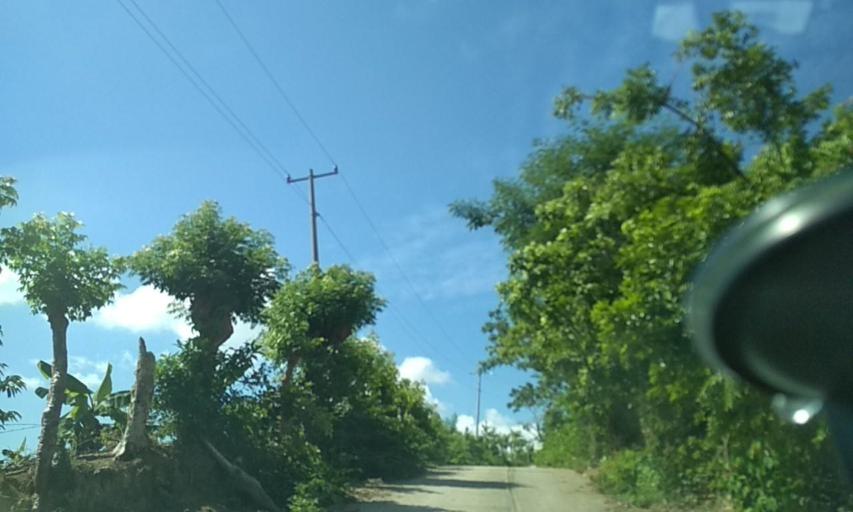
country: MX
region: Veracruz
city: Cazones de Herrera
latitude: 20.6217
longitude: -97.3228
